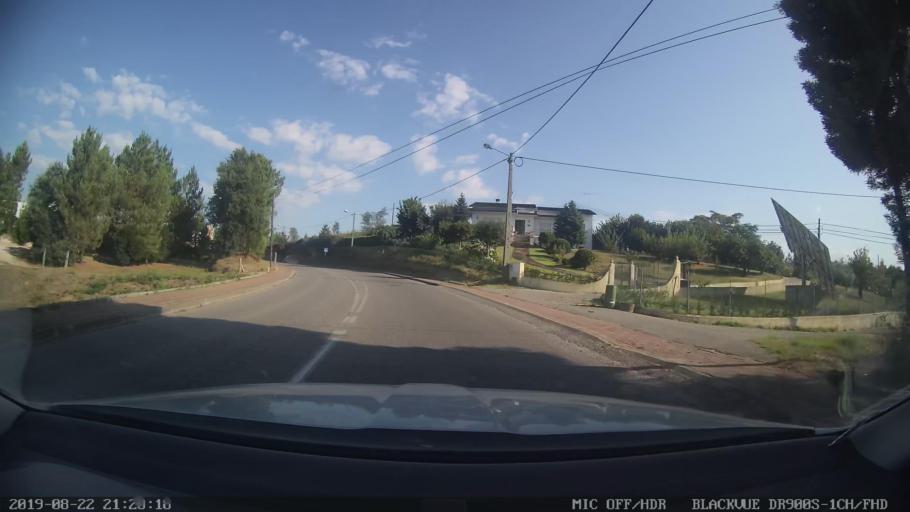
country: PT
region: Castelo Branco
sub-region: Serta
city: Serta
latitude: 39.8115
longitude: -8.1069
